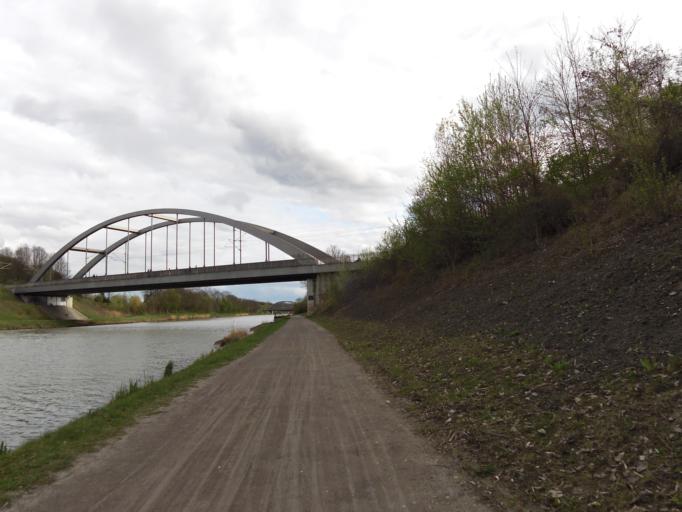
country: DE
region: Lower Saxony
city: Laatzen
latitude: 52.3756
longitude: 9.8474
